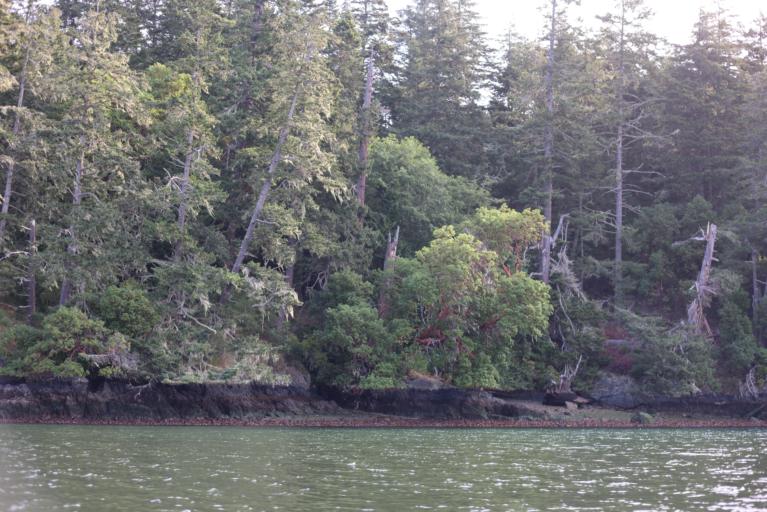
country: CA
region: British Columbia
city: Metchosin
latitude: 48.3434
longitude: -123.5584
